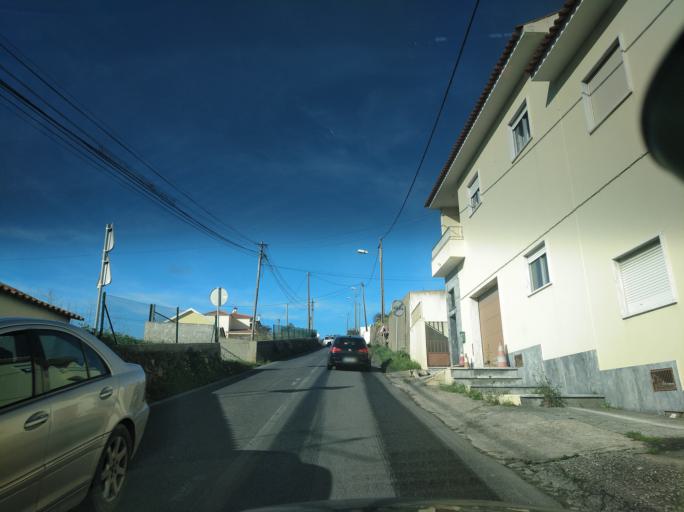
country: PT
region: Lisbon
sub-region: Sintra
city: Pero Pinheiro
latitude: 38.8898
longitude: -9.3267
